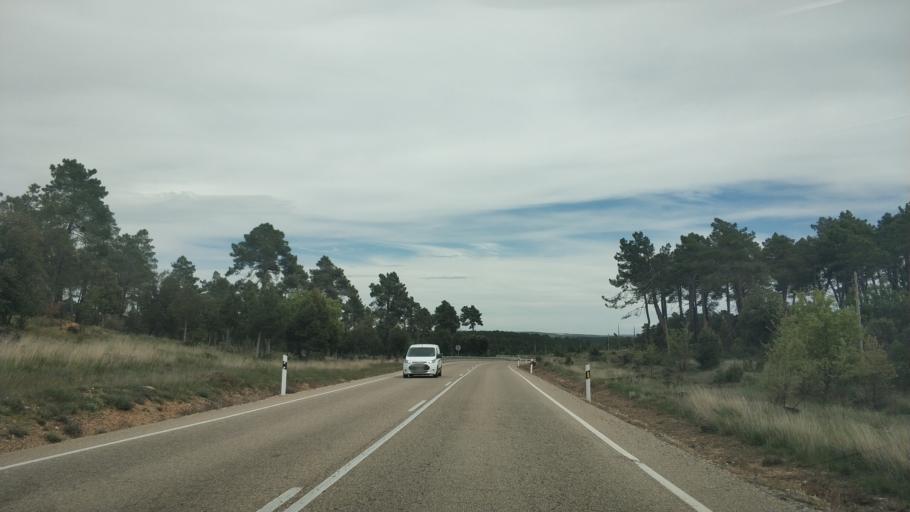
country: ES
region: Castille and Leon
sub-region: Provincia de Soria
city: Bayubas de Abajo
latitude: 41.5223
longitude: -2.9364
